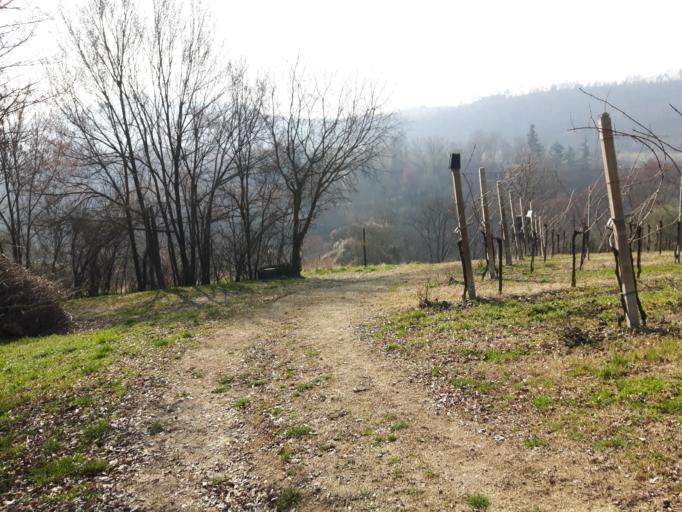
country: IT
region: Veneto
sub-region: Provincia di Padova
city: Vo
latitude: 45.3412
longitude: 11.6694
